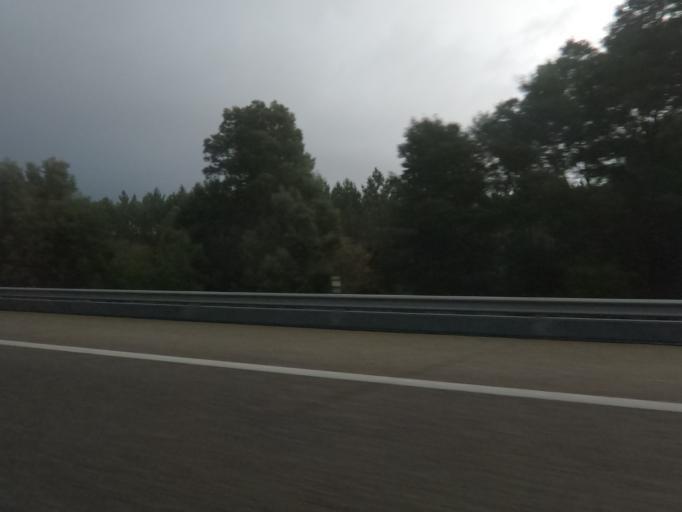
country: PT
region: Viana do Castelo
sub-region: Ponte de Lima
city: Ponte de Lima
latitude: 41.8168
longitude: -8.5996
